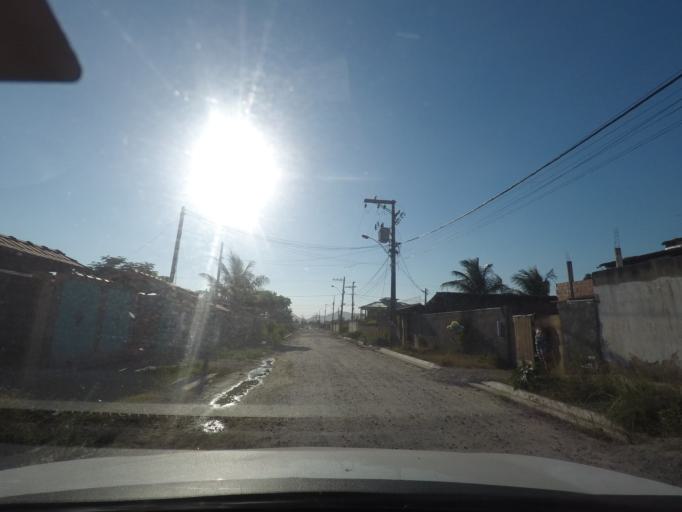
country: BR
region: Rio de Janeiro
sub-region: Marica
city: Marica
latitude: -22.9620
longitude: -42.9435
